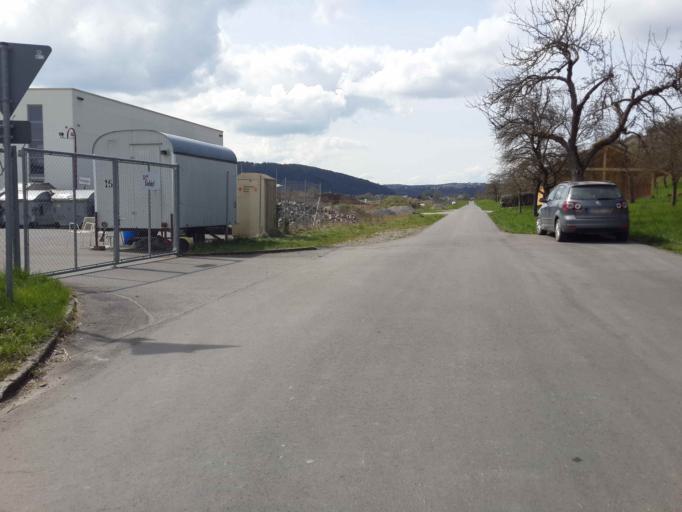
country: DE
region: Baden-Wuerttemberg
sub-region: Regierungsbezirk Stuttgart
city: Dorzbach
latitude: 49.3874
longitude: 9.6961
